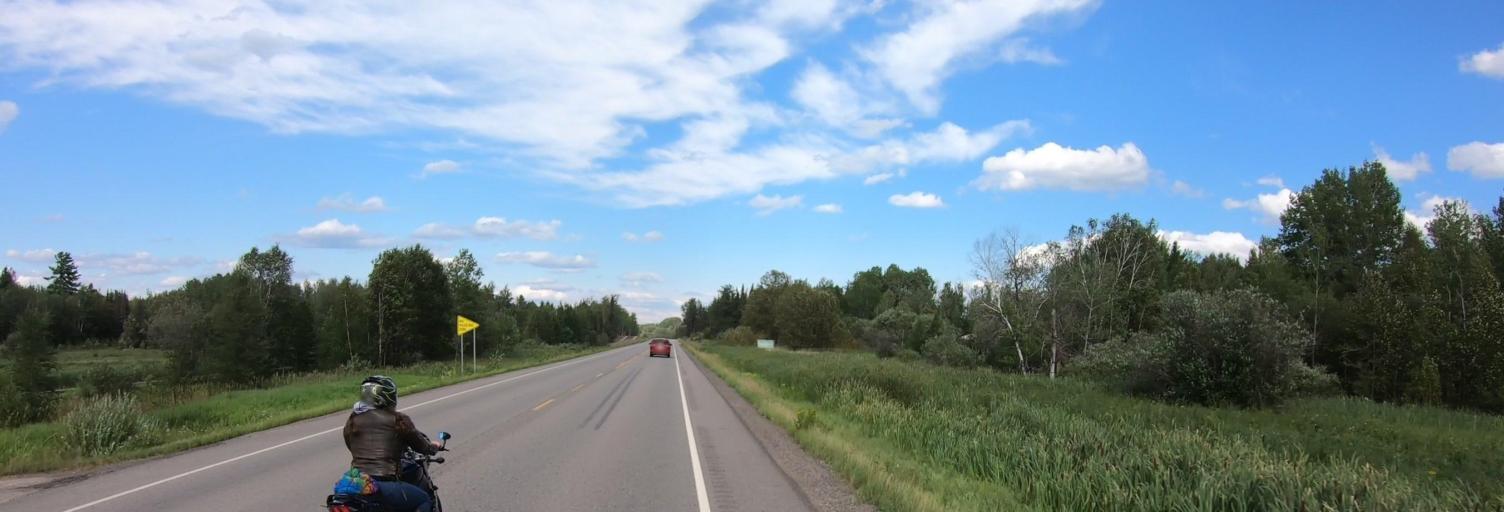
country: US
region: Minnesota
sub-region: Saint Louis County
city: Ely
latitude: 47.8832
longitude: -91.9584
